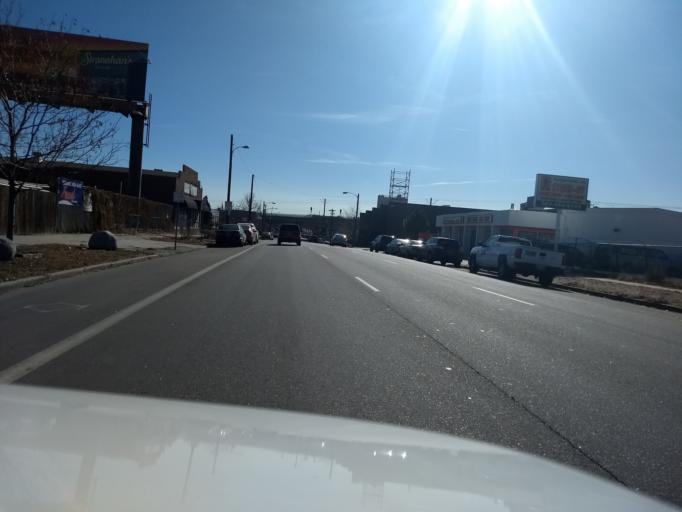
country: US
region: Colorado
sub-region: Denver County
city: Denver
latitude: 39.7224
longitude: -105.0001
